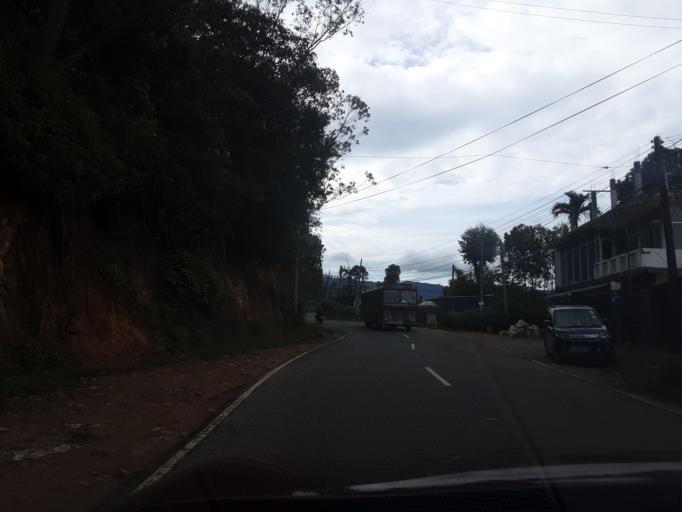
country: LK
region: Uva
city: Haputale
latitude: 6.8476
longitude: 80.9719
